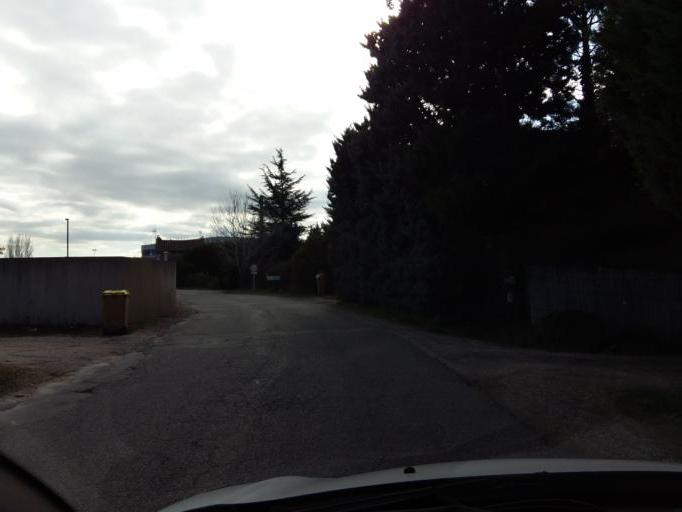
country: FR
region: Provence-Alpes-Cote d'Azur
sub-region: Departement du Vaucluse
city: Cheval-Blanc
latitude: 43.8117
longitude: 5.0483
